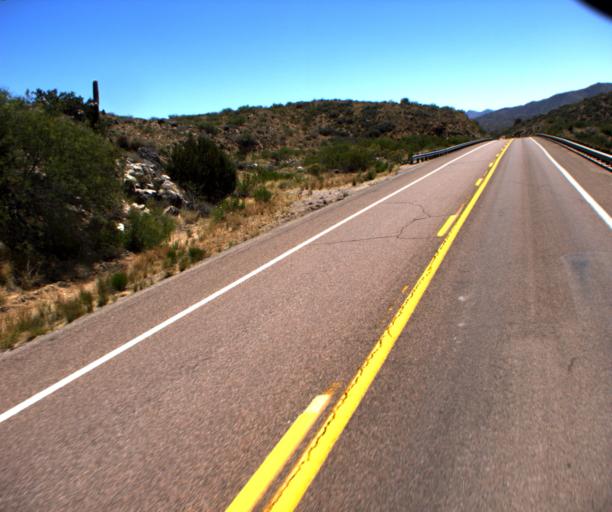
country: US
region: Arizona
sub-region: Yavapai County
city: Bagdad
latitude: 34.5520
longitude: -113.1528
